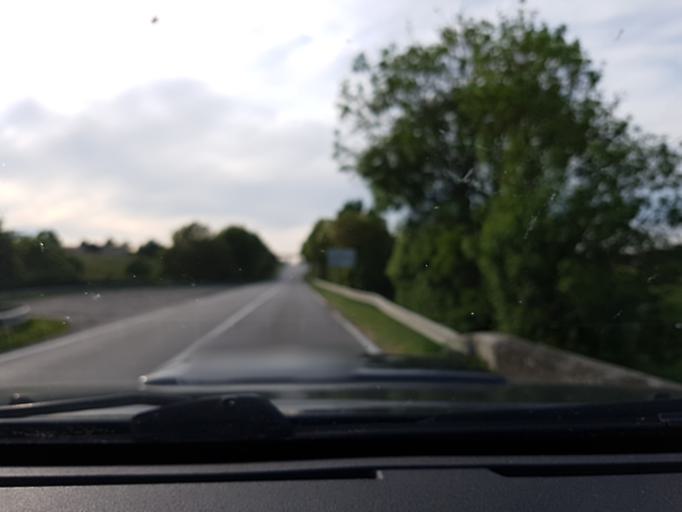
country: FR
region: Pays de la Loire
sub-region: Departement de la Vendee
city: Mache
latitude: 46.7698
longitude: -1.6656
